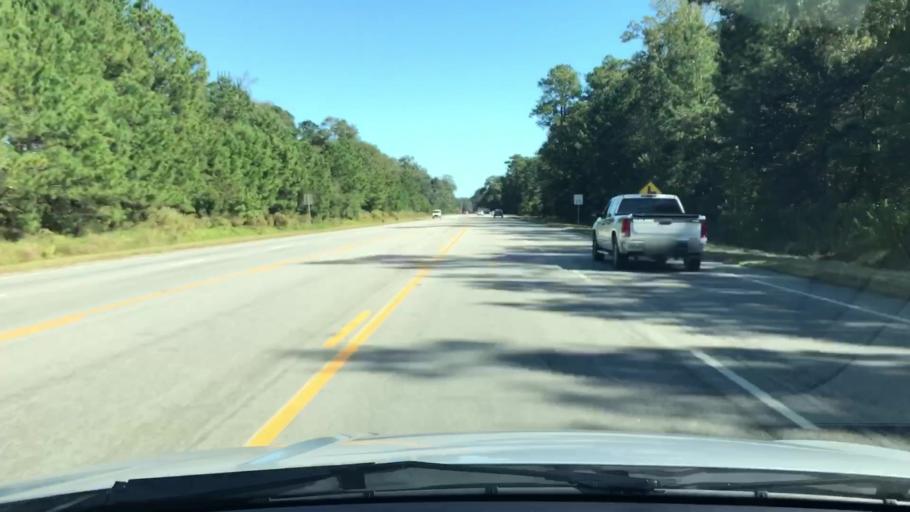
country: US
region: South Carolina
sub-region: Beaufort County
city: Bluffton
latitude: 32.3541
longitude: -80.9031
